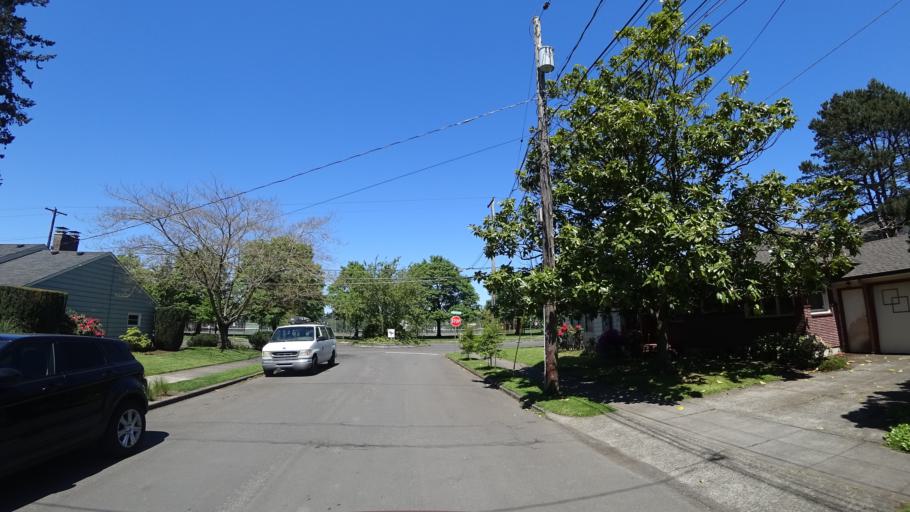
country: US
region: Oregon
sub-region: Multnomah County
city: Lents
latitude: 45.5011
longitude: -122.6050
